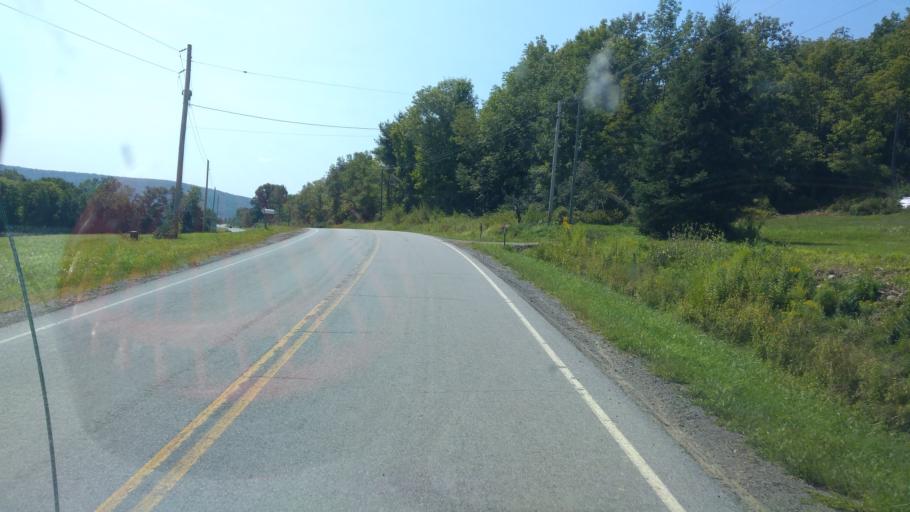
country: US
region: New York
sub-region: Allegany County
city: Belmont
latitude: 42.3188
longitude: -77.9525
